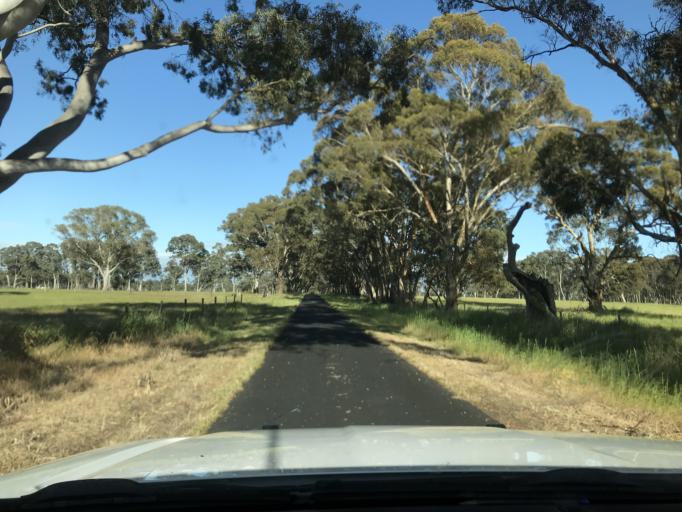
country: AU
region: South Australia
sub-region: Wattle Range
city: Penola
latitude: -37.2018
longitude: 140.9920
